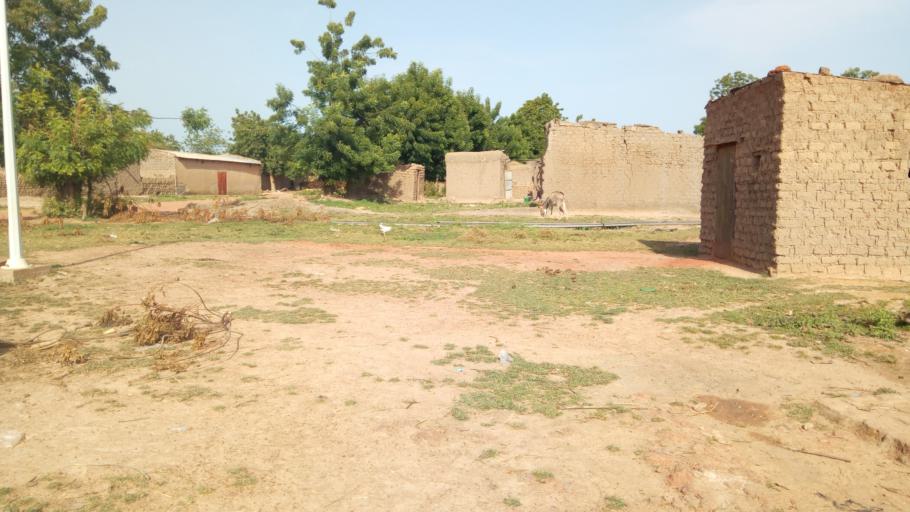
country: ML
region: Sikasso
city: Koutiala
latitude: 12.5388
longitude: -5.1649
